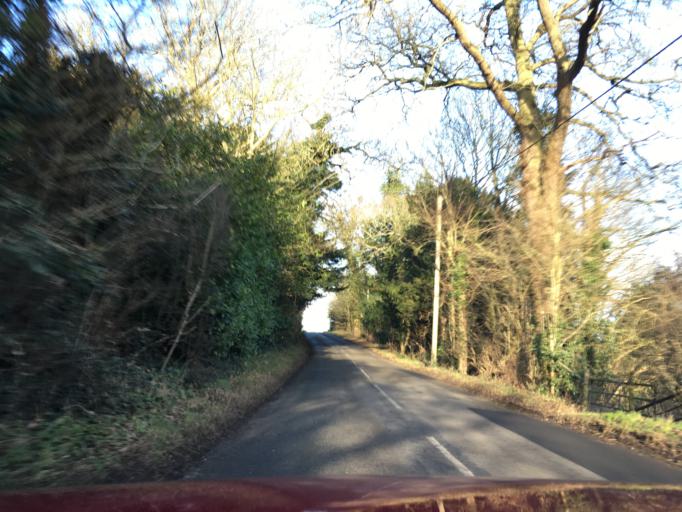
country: GB
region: England
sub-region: Warwickshire
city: Stratford-upon-Avon
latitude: 52.2304
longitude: -1.6881
